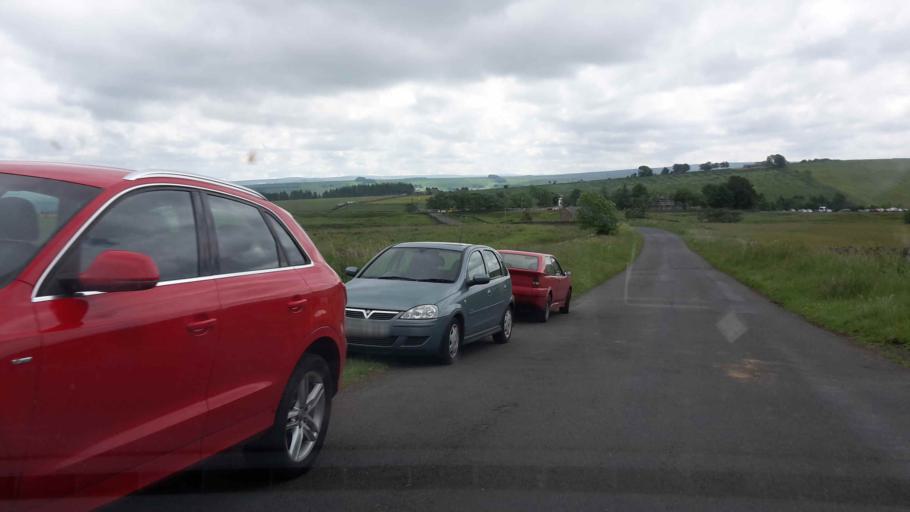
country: GB
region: England
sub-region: Northumberland
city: Bardon Mill
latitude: 54.9996
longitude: -2.3882
